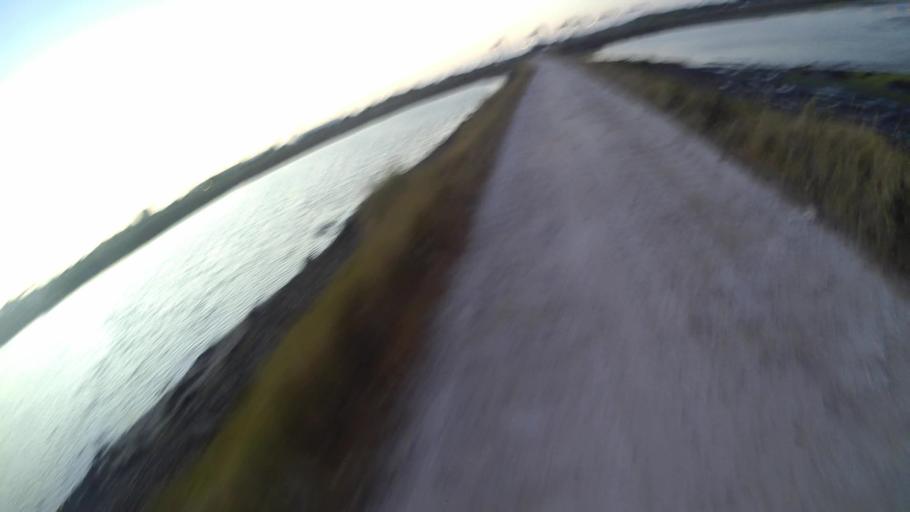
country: PT
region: Aveiro
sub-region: Aveiro
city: Aveiro
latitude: 40.6331
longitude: -8.6754
